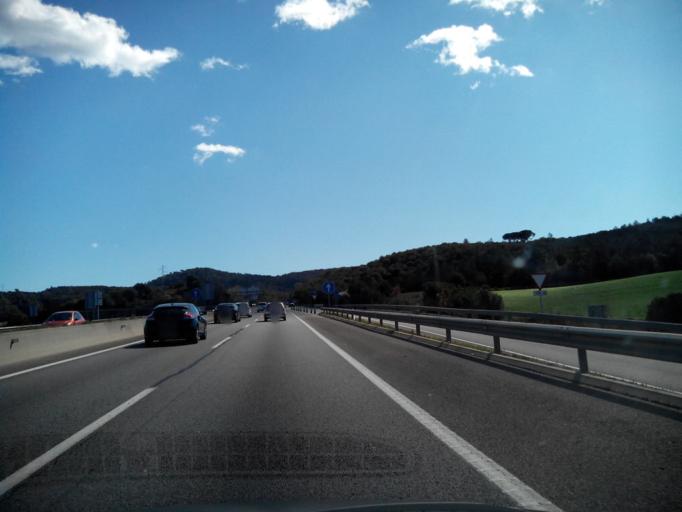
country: ES
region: Catalonia
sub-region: Provincia de Barcelona
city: La Roca del Valles
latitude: 41.5922
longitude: 2.3429
